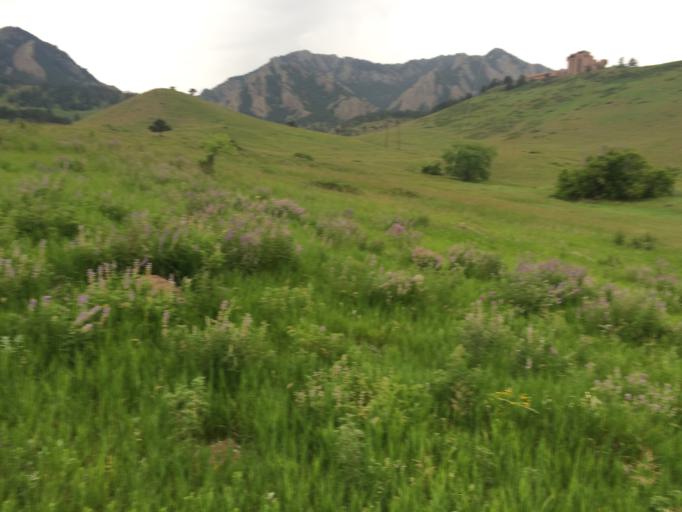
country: US
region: Colorado
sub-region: Boulder County
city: Boulder
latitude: 39.9754
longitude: -105.2675
